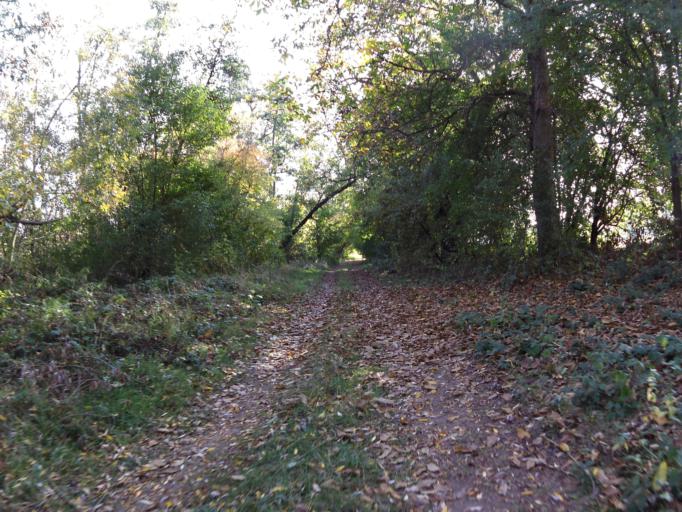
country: DE
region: Bavaria
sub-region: Regierungsbezirk Unterfranken
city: Eibelstadt
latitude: 49.7240
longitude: 9.9910
